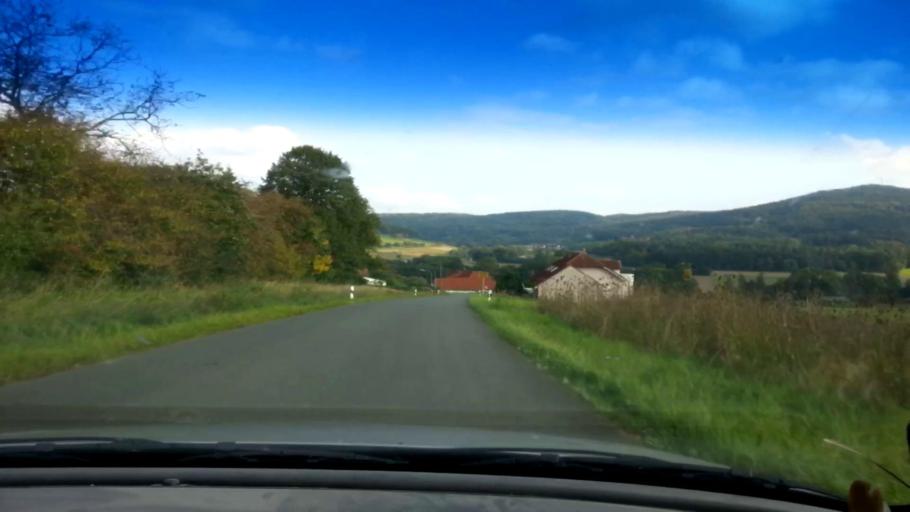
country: DE
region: Bavaria
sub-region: Upper Franconia
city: Schesslitz
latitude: 50.0076
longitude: 11.0572
